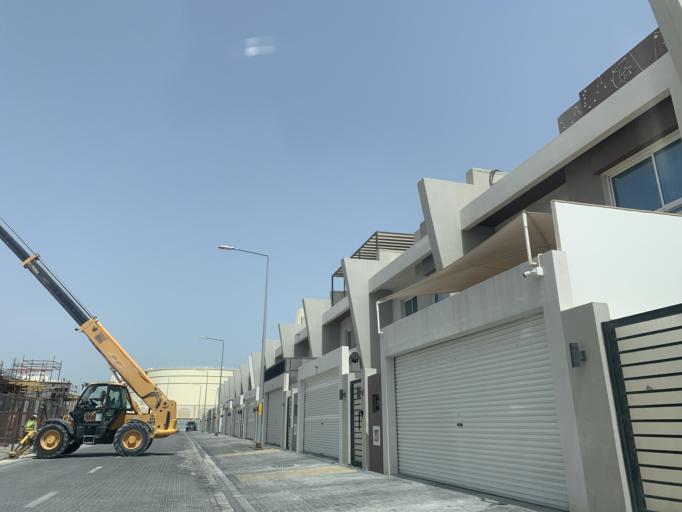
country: BH
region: Northern
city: Madinat `Isa
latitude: 26.1547
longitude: 50.5624
